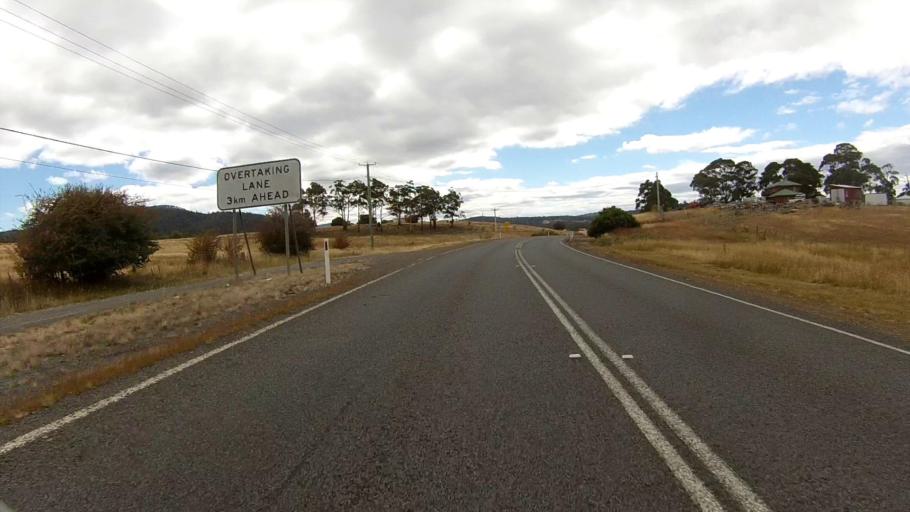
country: AU
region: Tasmania
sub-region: Sorell
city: Sorell
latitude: -42.6542
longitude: 147.5364
